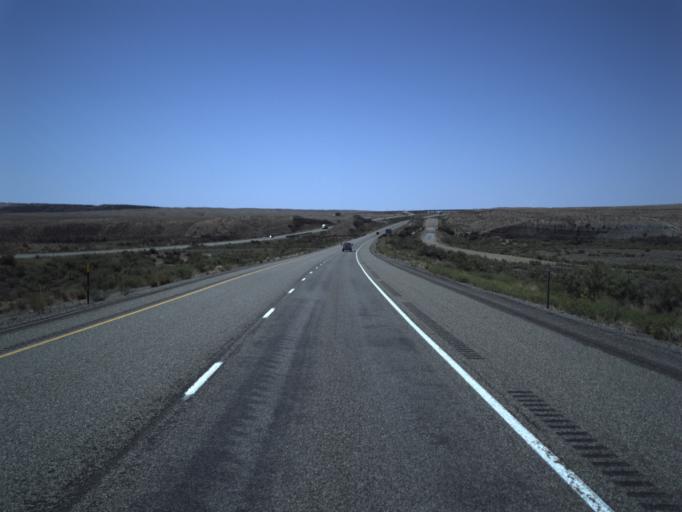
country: US
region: Colorado
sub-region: Mesa County
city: Loma
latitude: 39.1270
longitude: -109.1663
